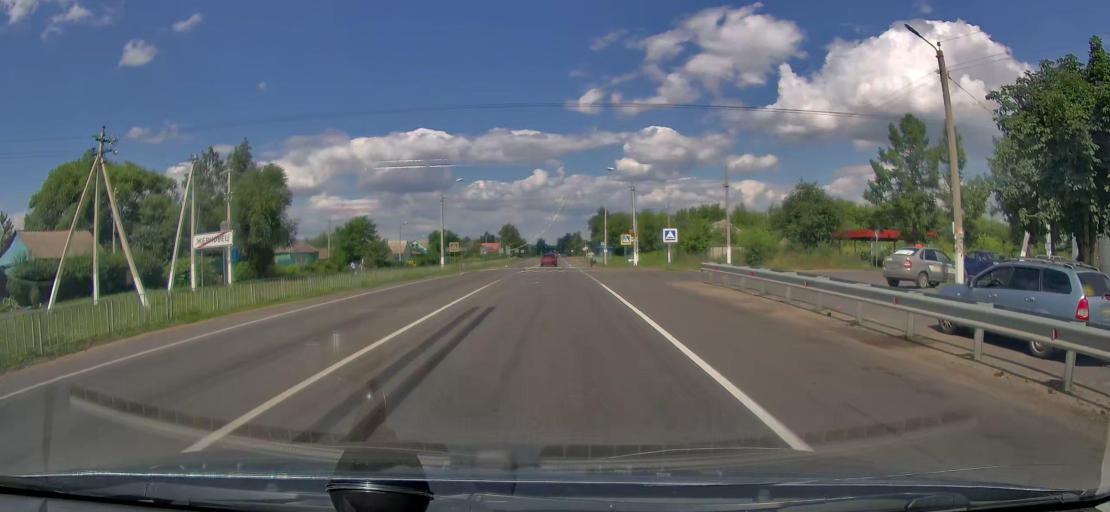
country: RU
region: Kursk
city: Zolotukhino
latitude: 51.9139
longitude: 36.3056
